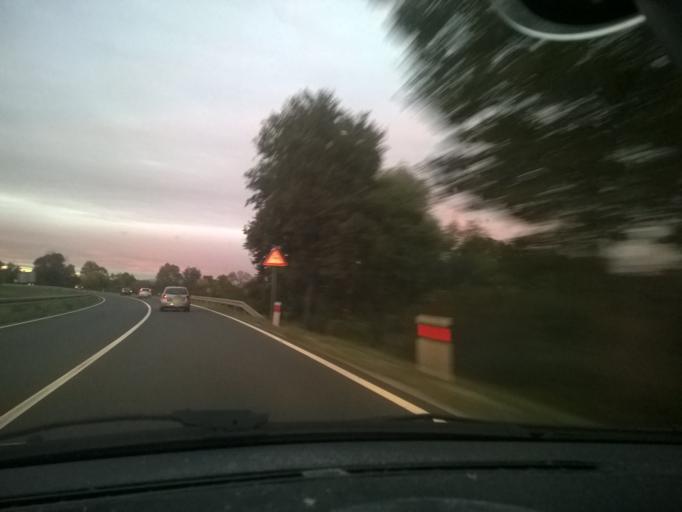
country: HR
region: Zagrebacka
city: Pojatno
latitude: 45.9233
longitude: 15.8230
